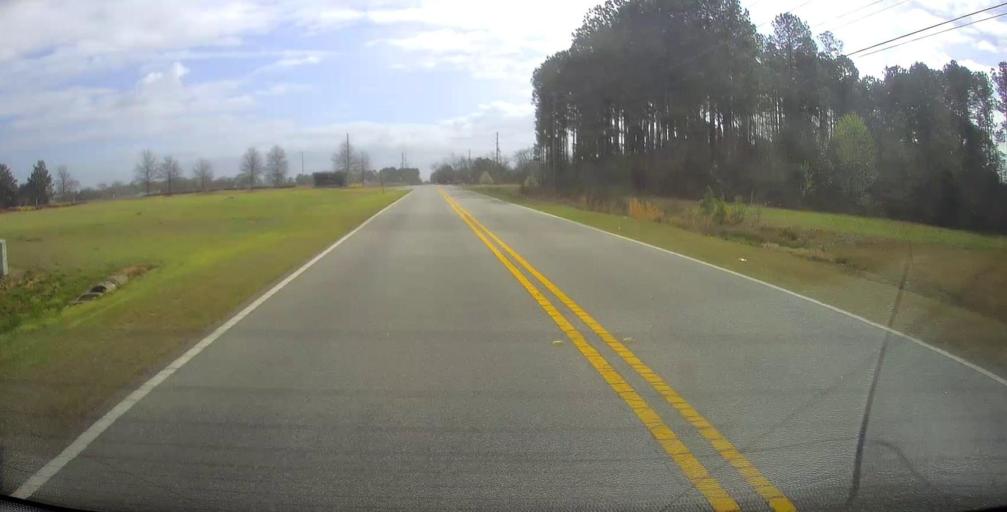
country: US
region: Georgia
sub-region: Houston County
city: Centerville
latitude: 32.6019
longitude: -83.6827
